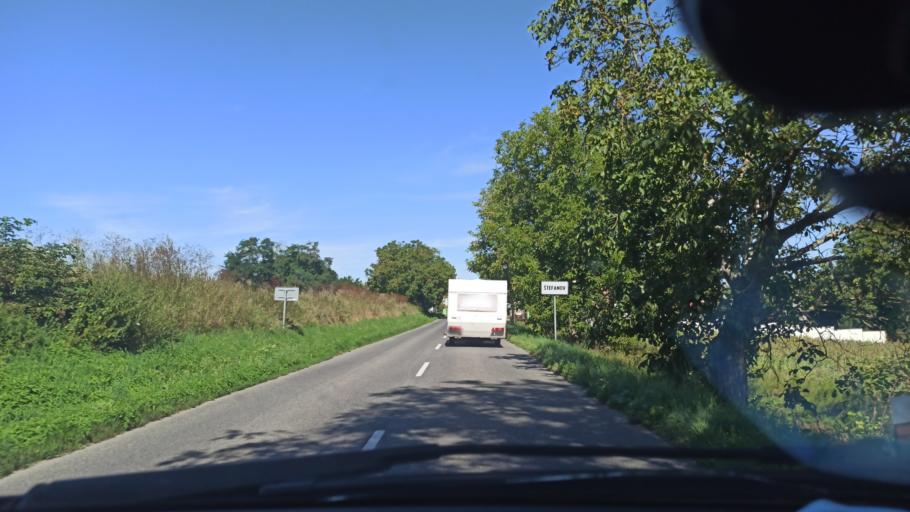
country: SK
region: Trnavsky
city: Gbely
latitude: 48.6699
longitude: 17.2033
